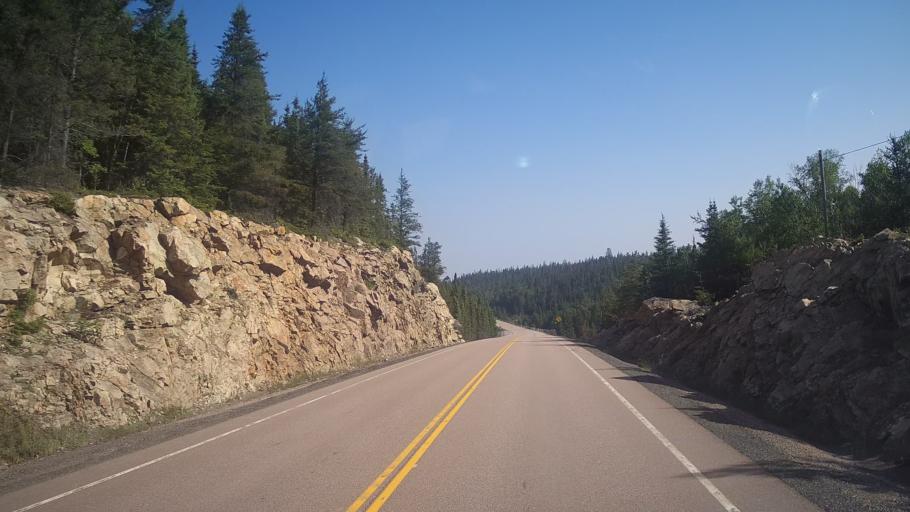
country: CA
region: Ontario
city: Rayside-Balfour
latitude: 46.9929
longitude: -81.6326
